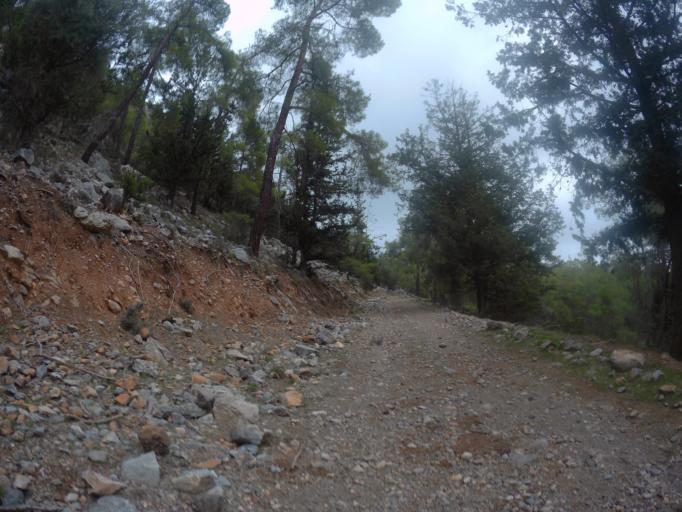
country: CY
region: Ammochostos
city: Lefkonoiko
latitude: 35.3024
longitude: 33.5756
